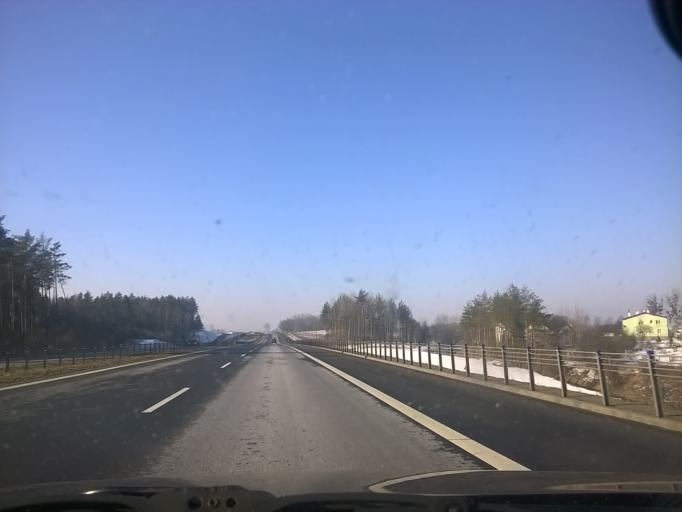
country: PL
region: Warmian-Masurian Voivodeship
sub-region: Powiat olsztynski
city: Biskupiec
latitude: 53.8449
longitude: 20.9917
